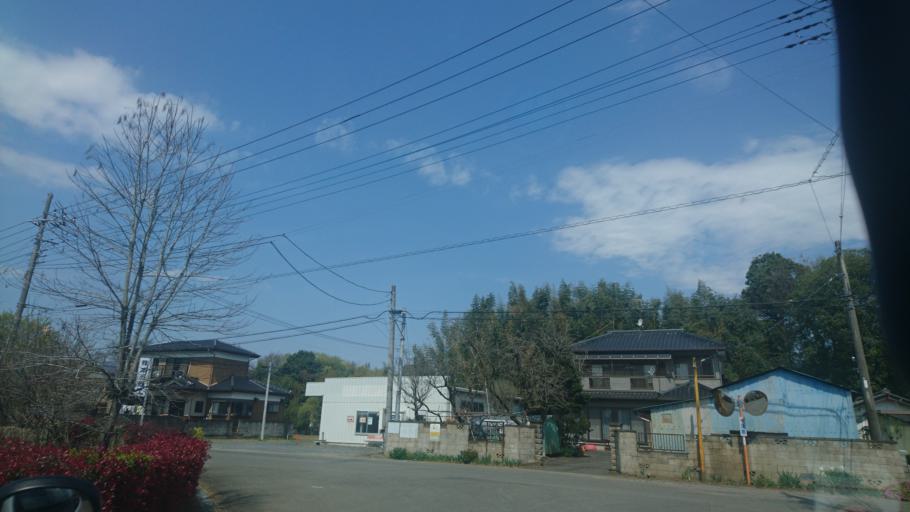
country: JP
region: Ibaraki
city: Yuki
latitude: 36.2407
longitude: 139.9239
